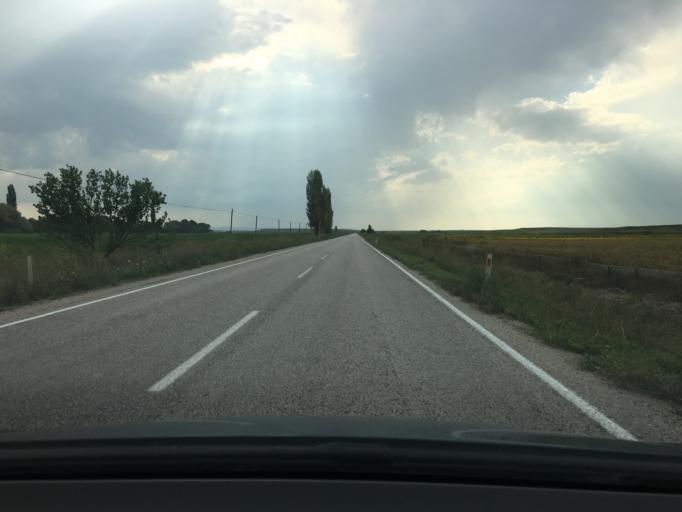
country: TR
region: Eskisehir
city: Mahmudiye
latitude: 39.5760
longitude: 30.9020
